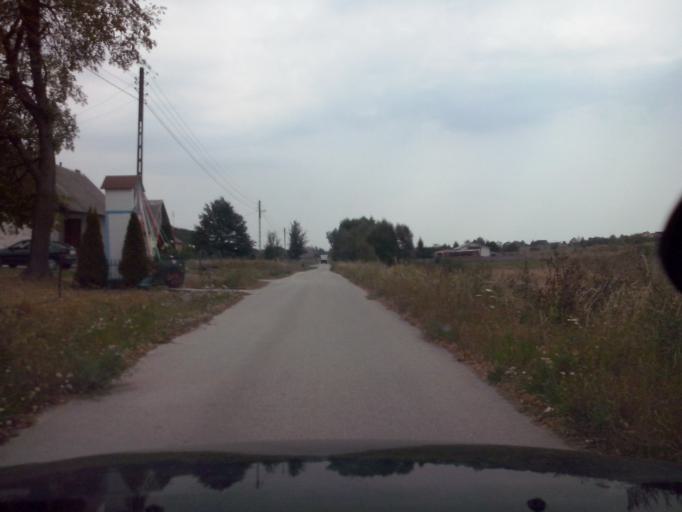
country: PL
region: Swietokrzyskie
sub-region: Powiat kielecki
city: Brzeziny
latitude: 50.7825
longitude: 20.5505
